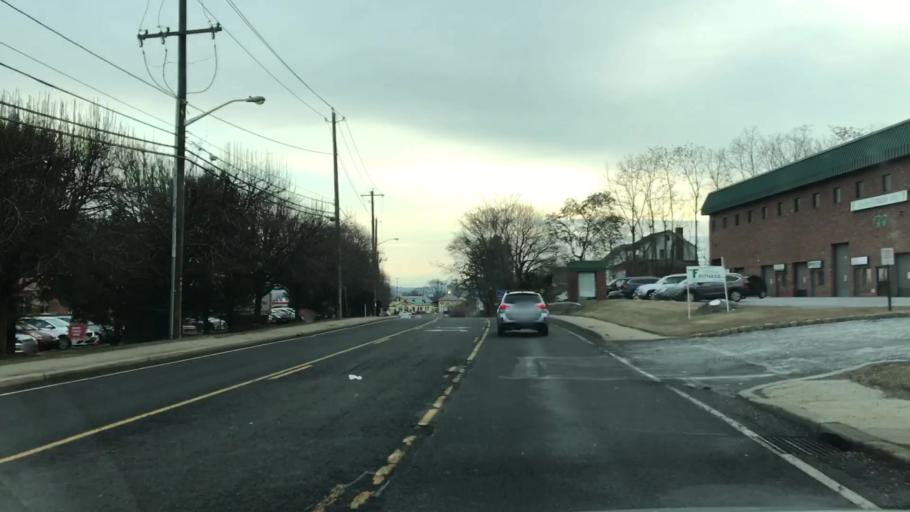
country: US
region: New York
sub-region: Rockland County
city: West Haverstraw
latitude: 41.1975
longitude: -73.9789
